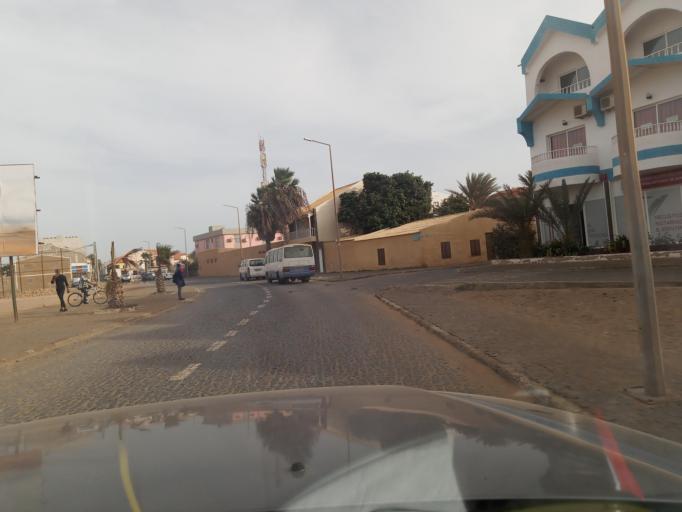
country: CV
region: Sal
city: Santa Maria
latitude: 16.6003
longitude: -22.9087
